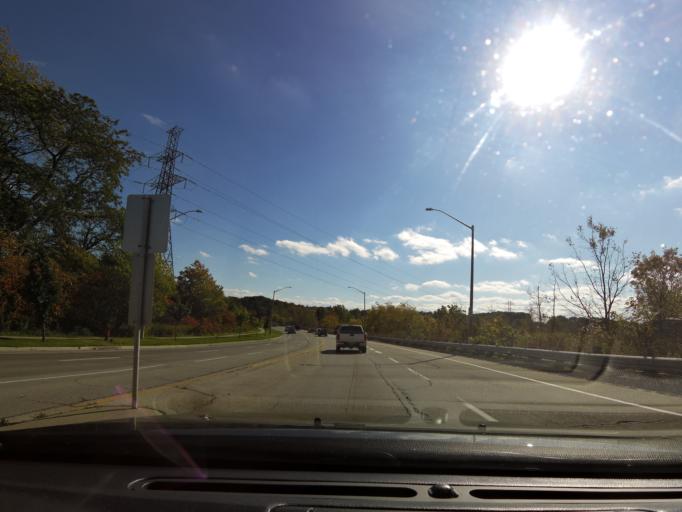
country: CA
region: Ontario
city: Ancaster
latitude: 43.2266
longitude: -79.9362
